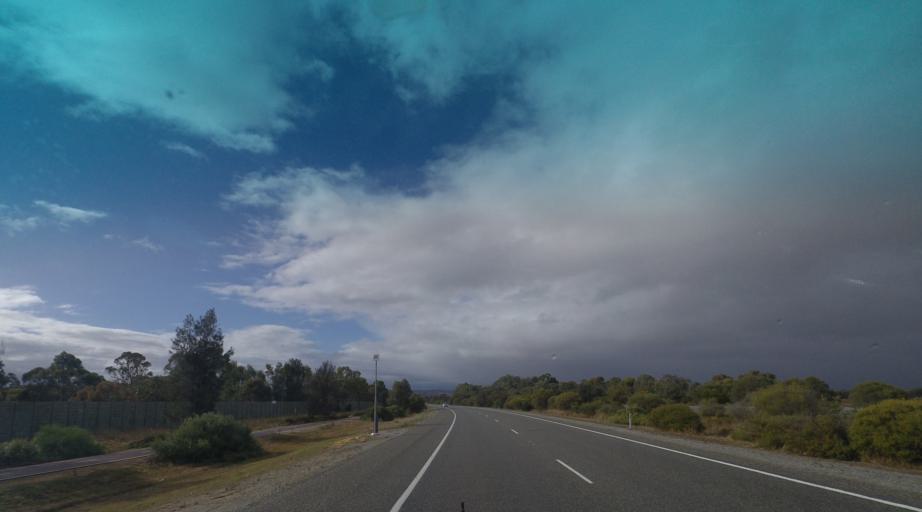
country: AU
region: Western Australia
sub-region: Serpentine-Jarrahdale
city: Oakford
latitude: -32.2011
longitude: 115.9647
